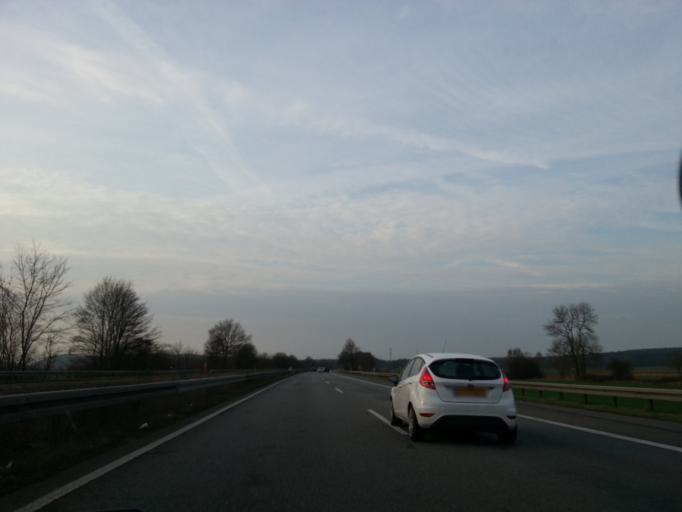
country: DE
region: North Rhine-Westphalia
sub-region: Regierungsbezirk Dusseldorf
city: Emmerich
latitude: 51.8656
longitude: 6.2217
